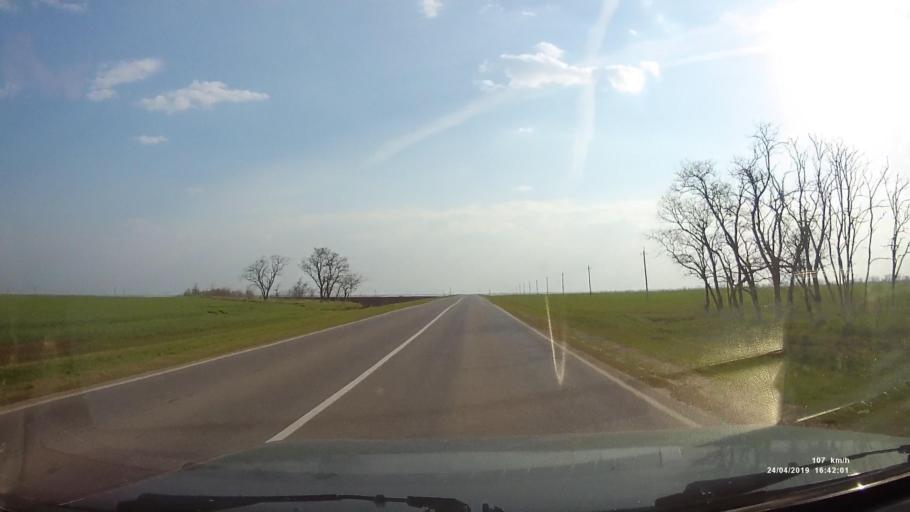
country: RU
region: Rostov
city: Gundorovskiy
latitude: 46.8125
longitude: 41.8590
